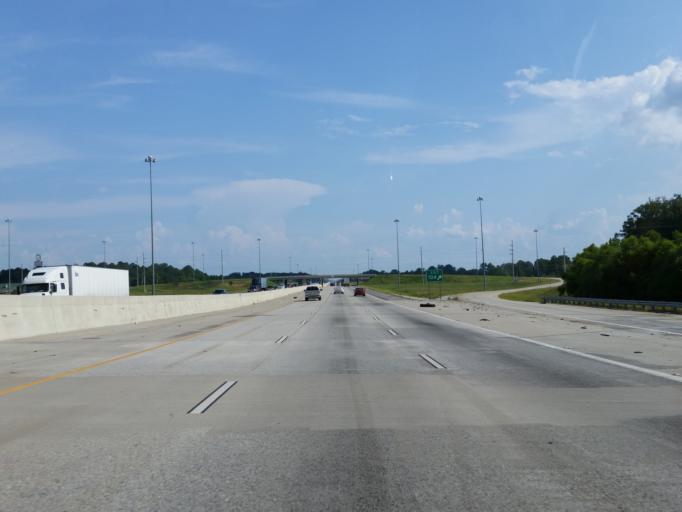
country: US
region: Georgia
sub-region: Crisp County
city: Cordele
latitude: 32.0093
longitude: -83.7595
